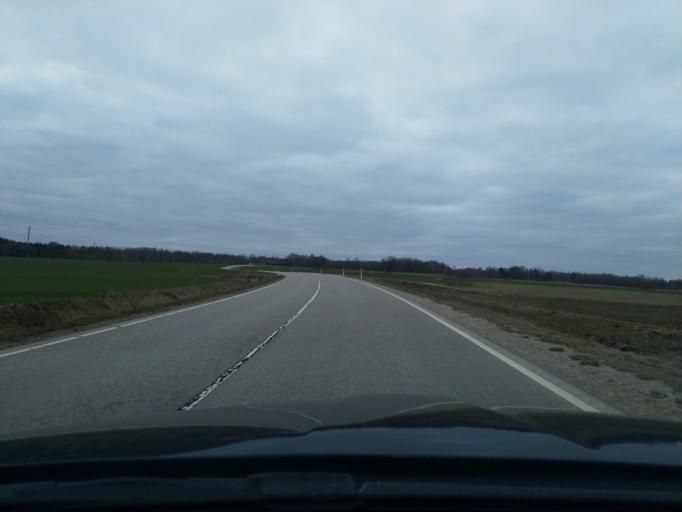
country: LV
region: Talsu Rajons
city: Sabile
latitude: 56.9415
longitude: 22.4909
